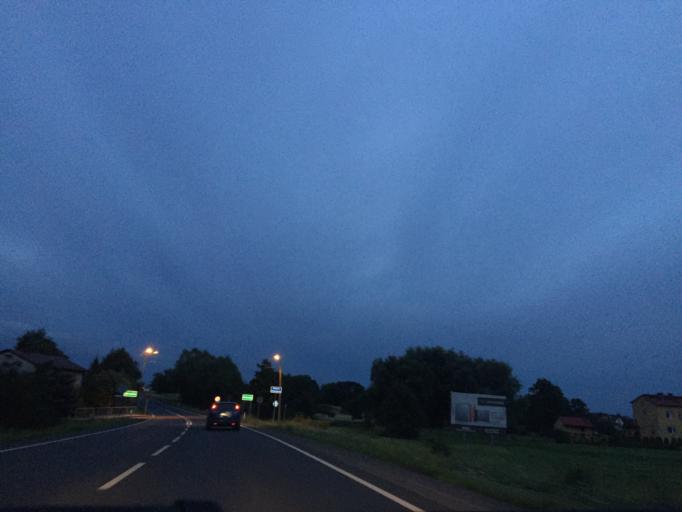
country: PL
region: Lesser Poland Voivodeship
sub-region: Powiat oswiecimski
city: Zaborze
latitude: 50.0233
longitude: 19.2333
